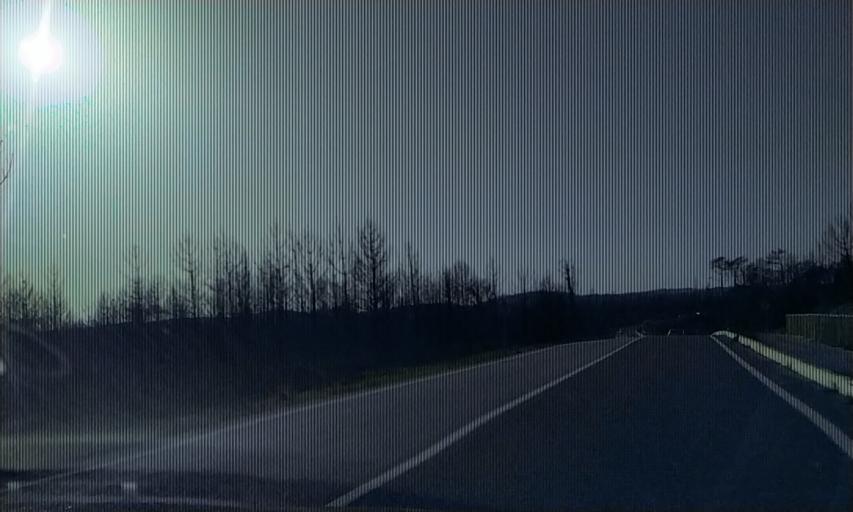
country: PT
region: Leiria
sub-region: Marinha Grande
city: Marinha Grande
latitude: 39.7464
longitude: -8.9716
